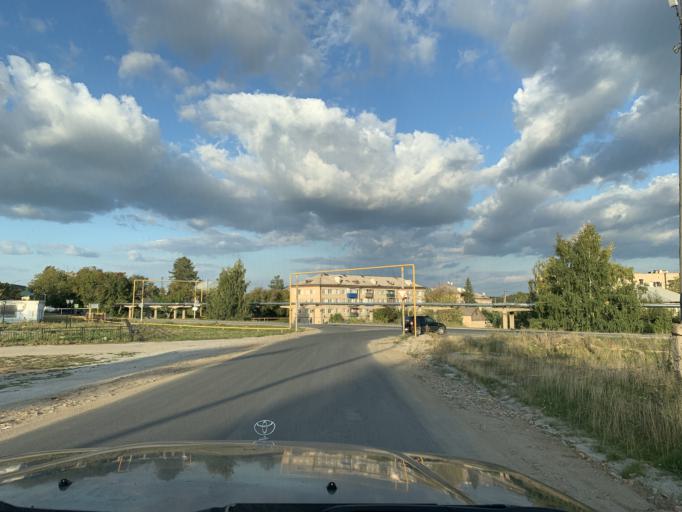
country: RU
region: Chelyabinsk
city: Vishnevogorsk
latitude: 55.9977
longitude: 60.6548
